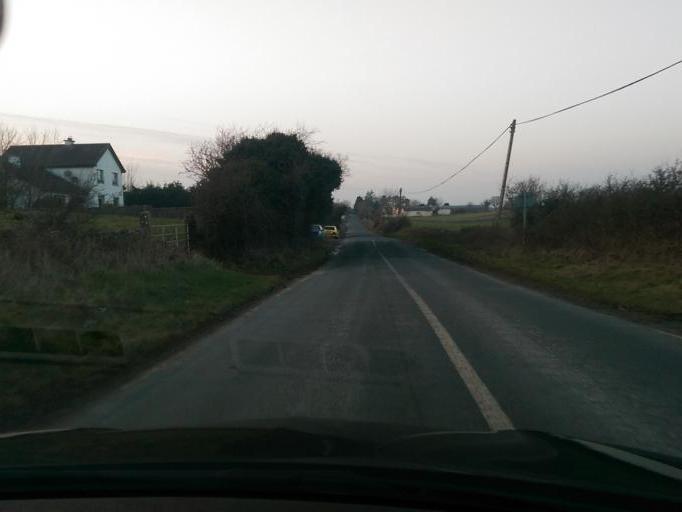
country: IE
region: Connaught
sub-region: County Galway
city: Athenry
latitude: 53.2681
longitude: -8.6916
